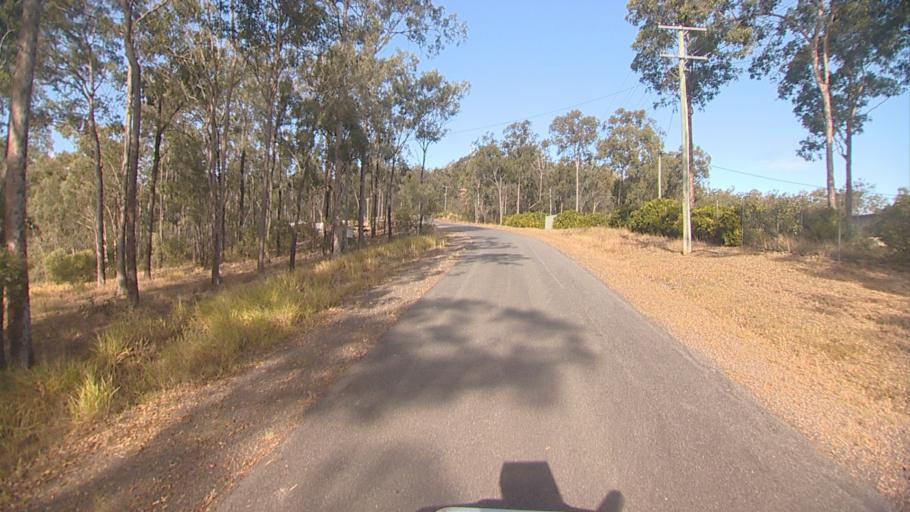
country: AU
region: Queensland
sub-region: Logan
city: Cedar Vale
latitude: -27.8454
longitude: 153.0714
